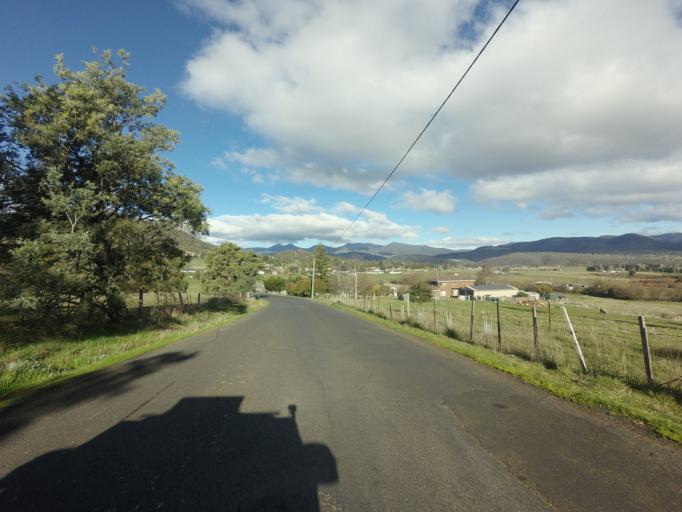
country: AU
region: Tasmania
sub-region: Derwent Valley
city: New Norfolk
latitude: -42.7515
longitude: 147.0468
